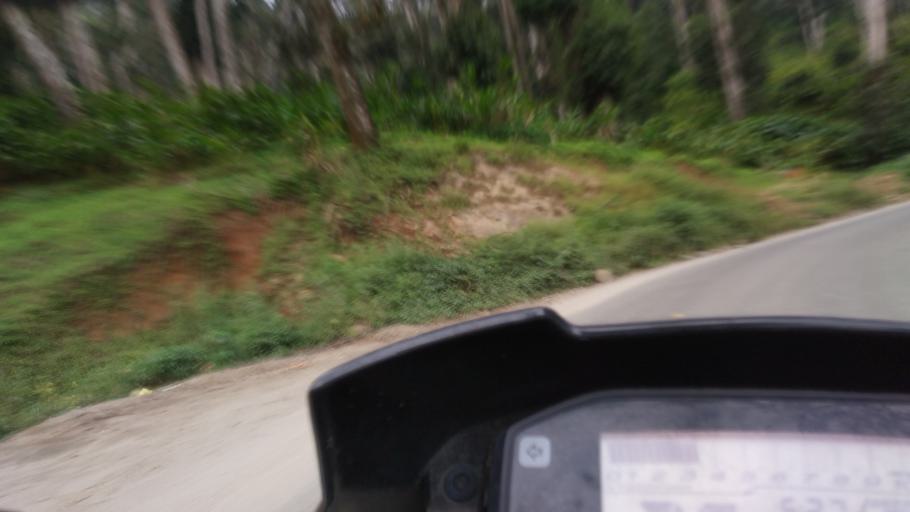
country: IN
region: Tamil Nadu
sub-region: Theni
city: Bodinayakkanur
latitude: 9.9990
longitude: 77.2219
